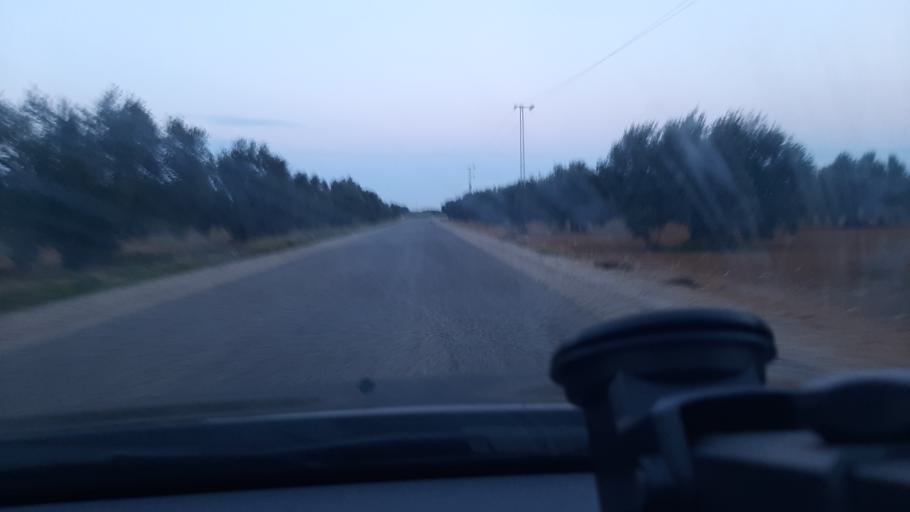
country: TN
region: Al Mahdiyah
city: Shurban
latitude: 35.0270
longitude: 10.4762
